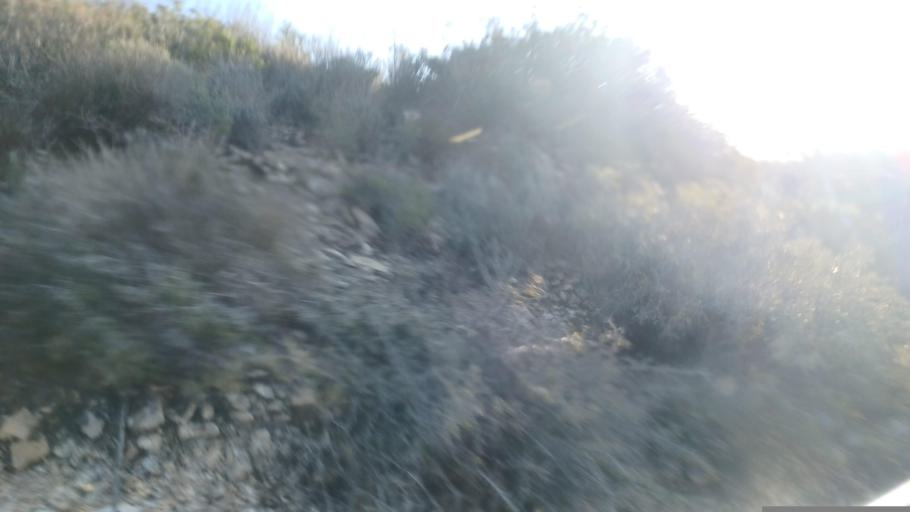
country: CY
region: Larnaka
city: Kofinou
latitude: 34.8351
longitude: 33.3051
